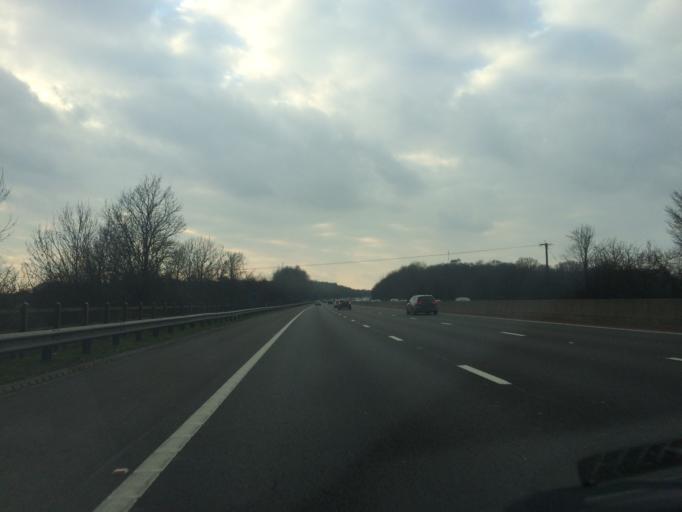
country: GB
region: England
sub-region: West Berkshire
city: Lambourn
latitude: 51.4732
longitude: -1.5357
